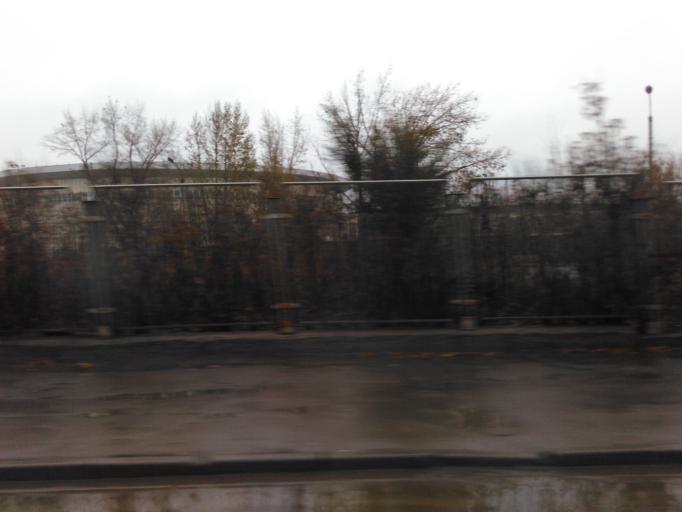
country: RU
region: Tatarstan
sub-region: Gorod Kazan'
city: Kazan
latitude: 55.7949
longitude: 49.0949
